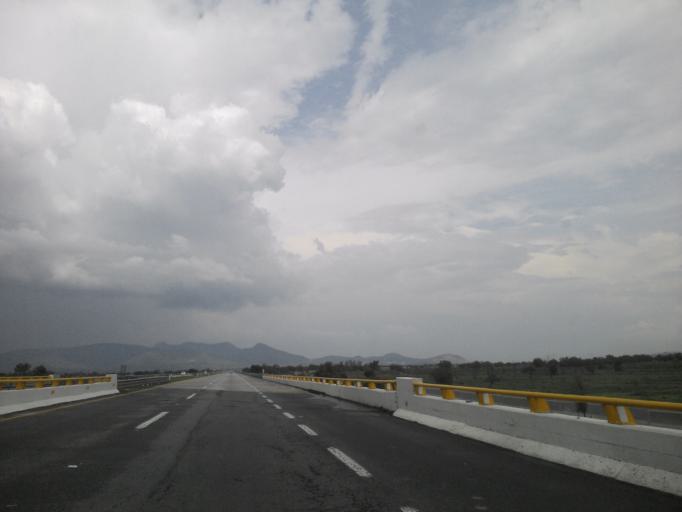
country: MX
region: Hidalgo
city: Doxey
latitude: 20.0870
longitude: -99.2580
